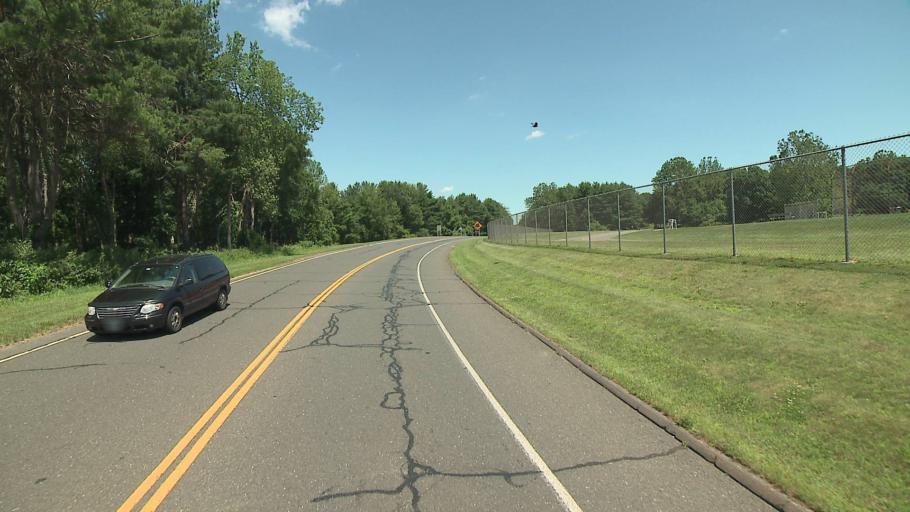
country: US
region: Connecticut
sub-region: Fairfield County
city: Newtown
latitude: 41.4038
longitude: -73.2855
